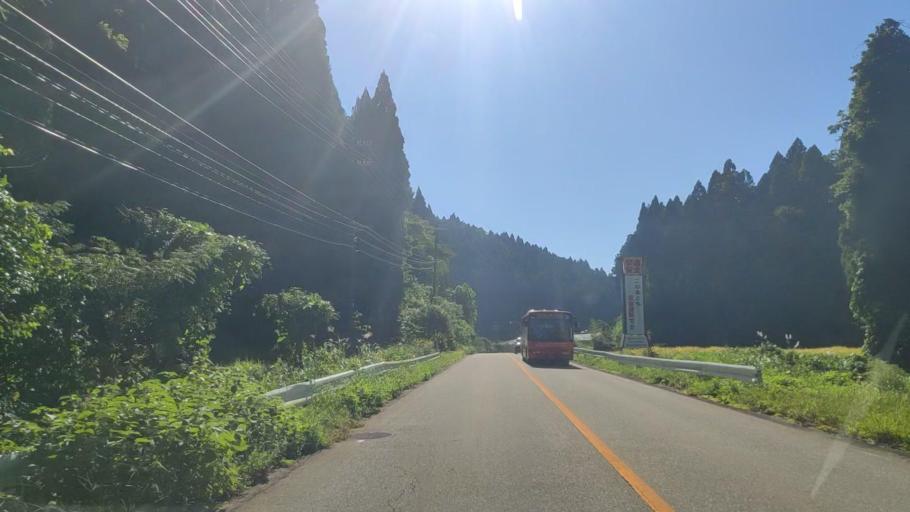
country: JP
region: Ishikawa
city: Nanao
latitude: 37.3289
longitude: 137.2075
